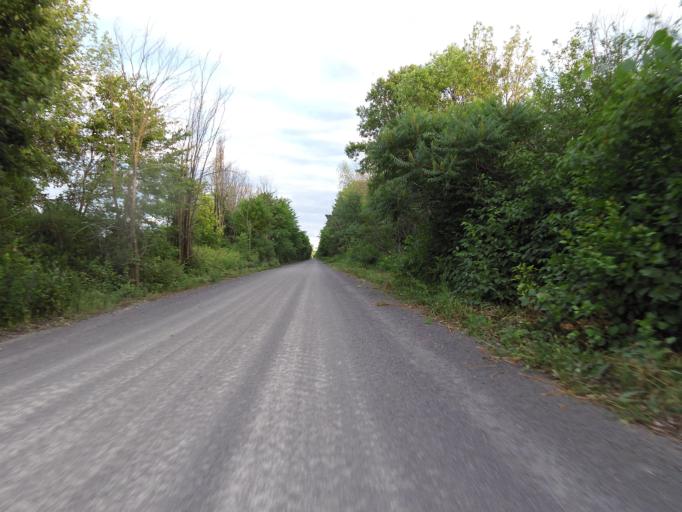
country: CA
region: Ontario
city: Arnprior
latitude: 45.3396
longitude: -76.2976
